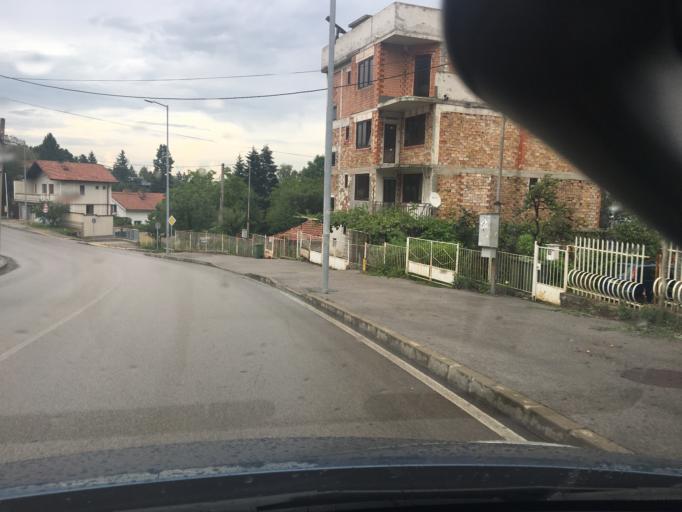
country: BG
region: Sofia-Capital
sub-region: Stolichna Obshtina
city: Sofia
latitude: 42.6315
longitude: 23.3059
